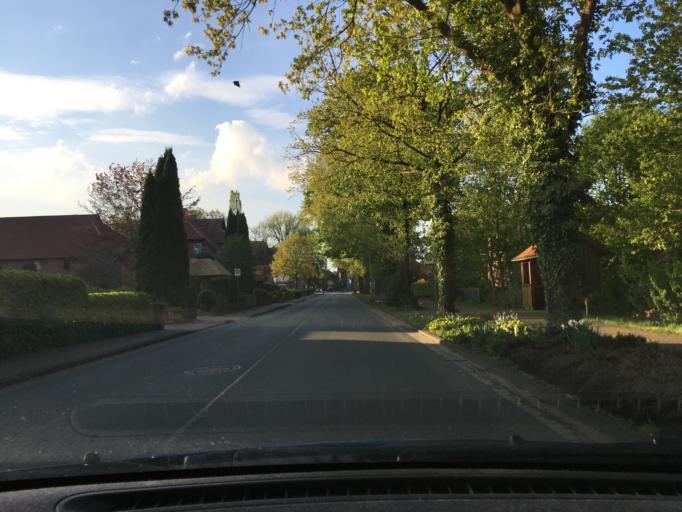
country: DE
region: Lower Saxony
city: Wietzendorf
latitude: 52.9152
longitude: 9.9768
